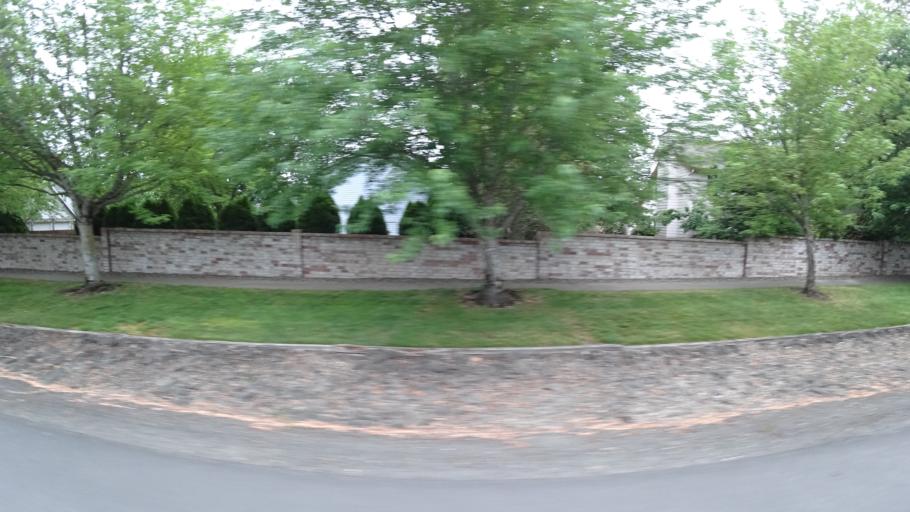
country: US
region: Oregon
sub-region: Washington County
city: Bethany
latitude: 45.5565
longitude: -122.8614
